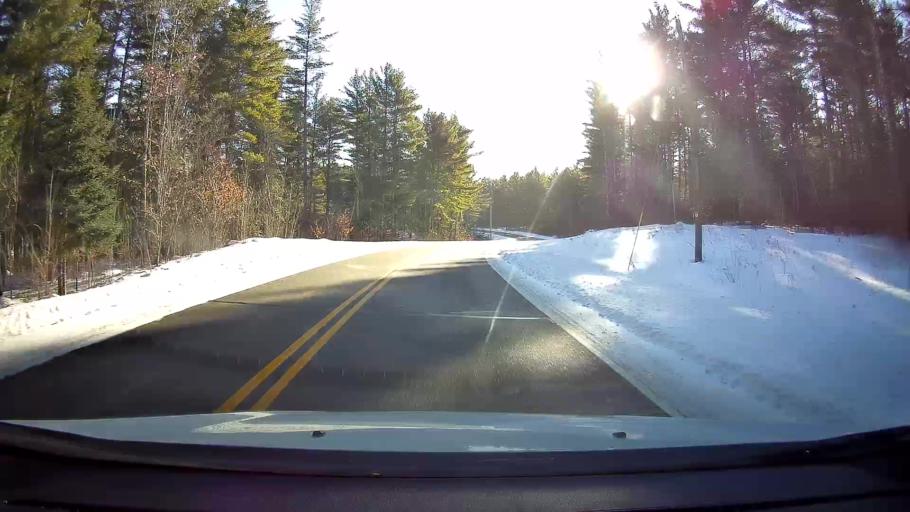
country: US
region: Wisconsin
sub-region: Sawyer County
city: Little Round Lake
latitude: 46.1133
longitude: -91.3168
